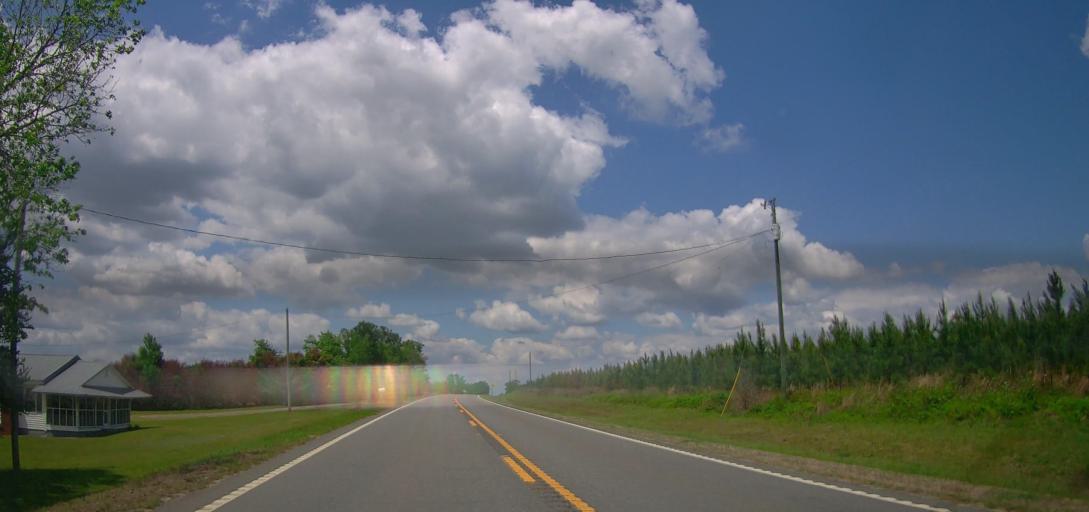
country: US
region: Georgia
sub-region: Treutlen County
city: Soperton
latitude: 32.4008
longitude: -82.6045
